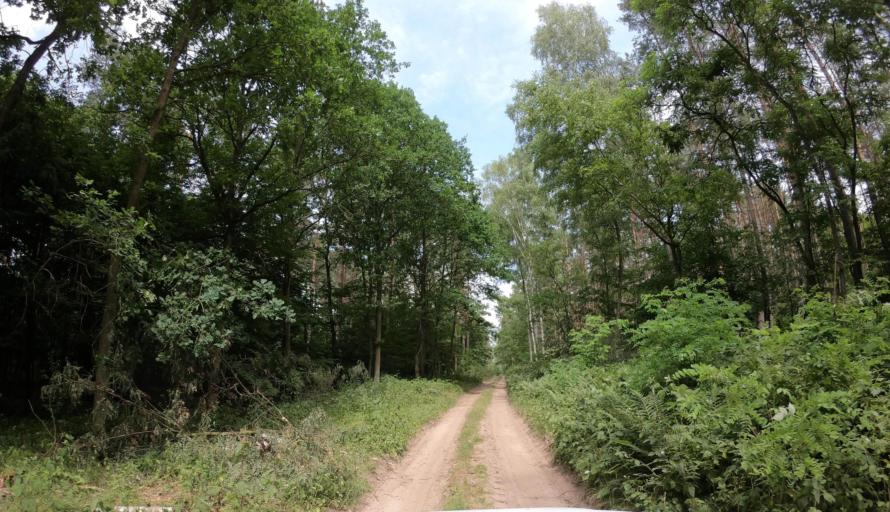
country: PL
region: West Pomeranian Voivodeship
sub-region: Powiat pyrzycki
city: Kozielice
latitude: 53.0217
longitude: 14.7468
